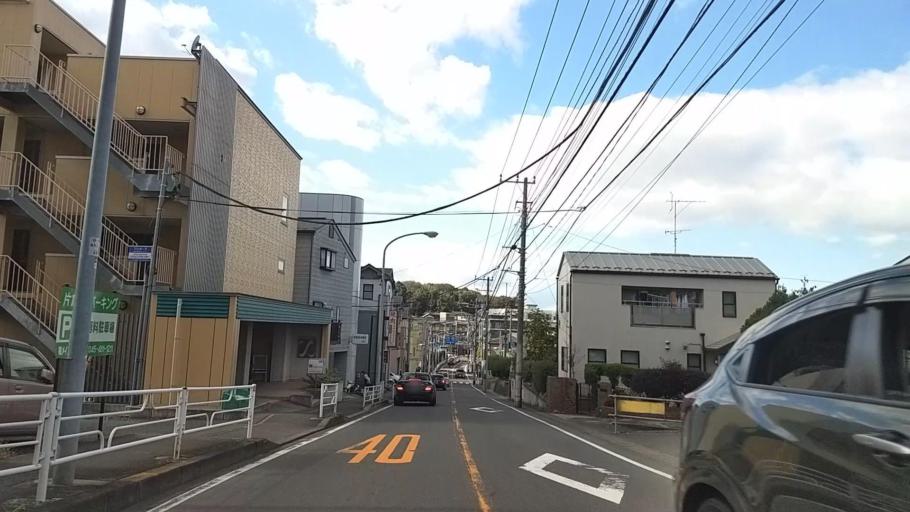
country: JP
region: Kanagawa
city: Yokohama
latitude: 35.4916
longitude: 139.6100
